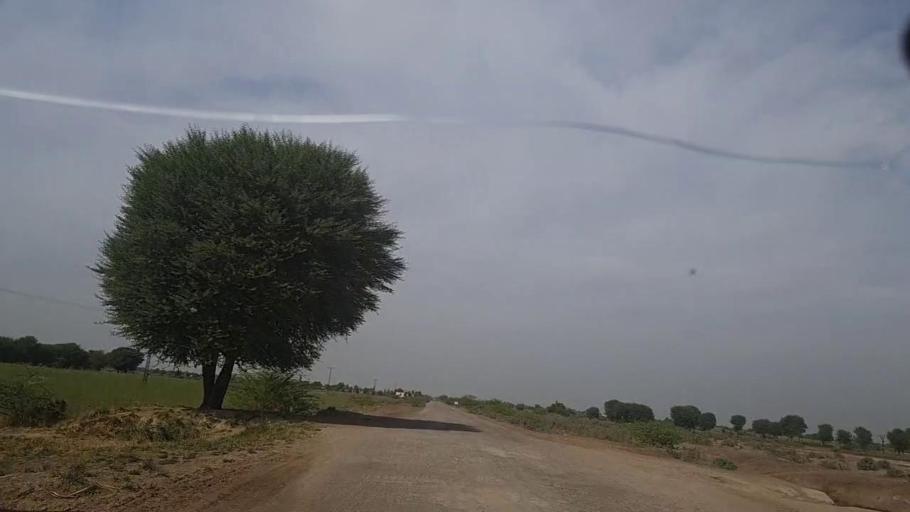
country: PK
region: Sindh
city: Pithoro
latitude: 25.5587
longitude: 69.3629
